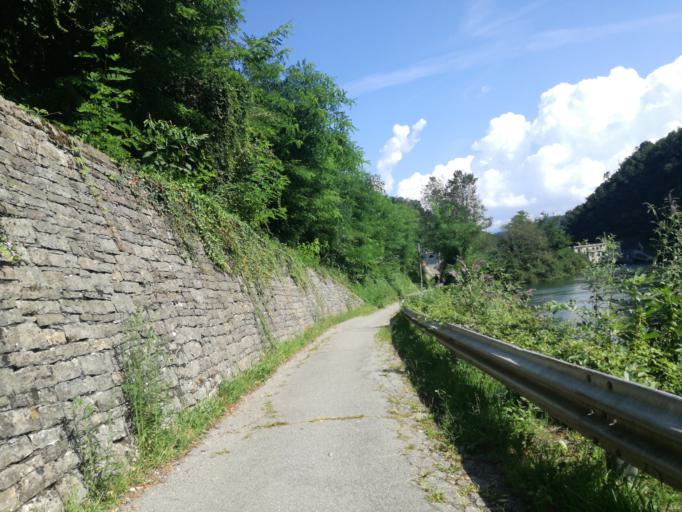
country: IT
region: Lombardy
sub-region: Provincia di Lecco
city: Paderno d'Adda
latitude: 45.6841
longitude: 9.4503
